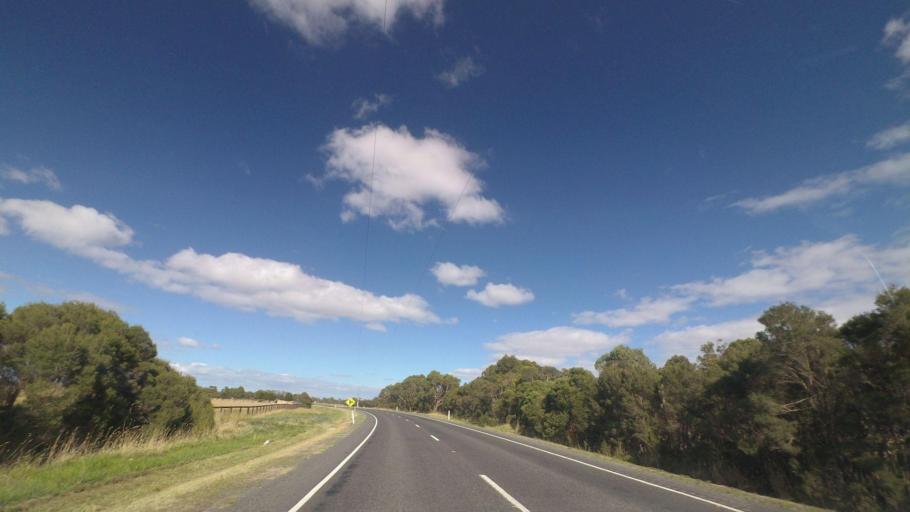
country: AU
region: Victoria
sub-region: Cardinia
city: Koo-Wee-Rup
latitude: -38.1872
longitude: 145.5309
